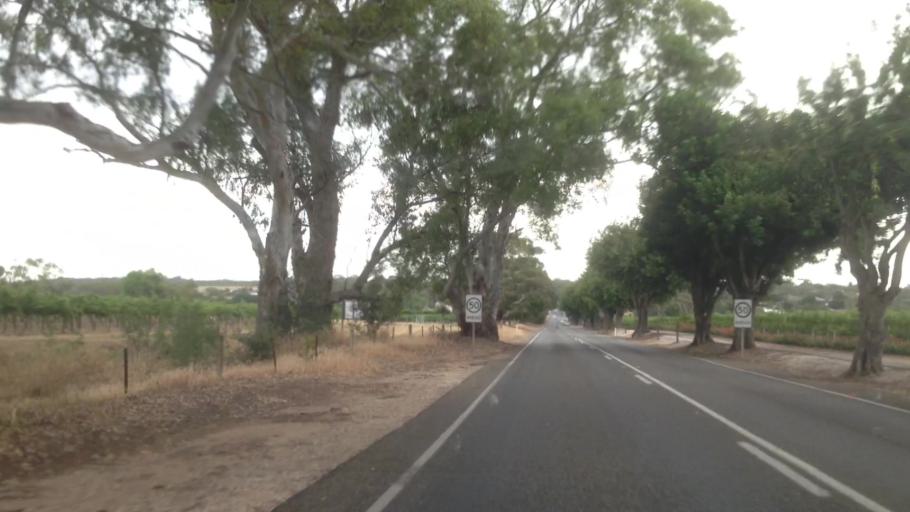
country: AU
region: South Australia
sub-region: Barossa
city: Lyndoch
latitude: -34.5994
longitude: 138.8981
